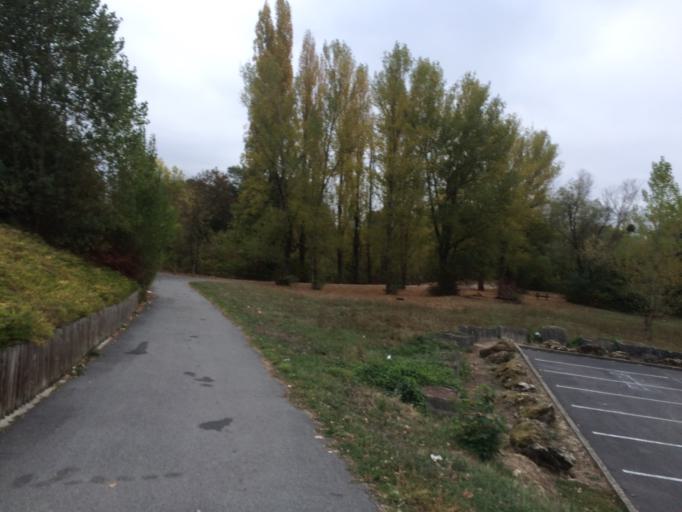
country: FR
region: Ile-de-France
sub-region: Departement de l'Essonne
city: Courcouronnes
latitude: 48.6284
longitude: 2.4038
